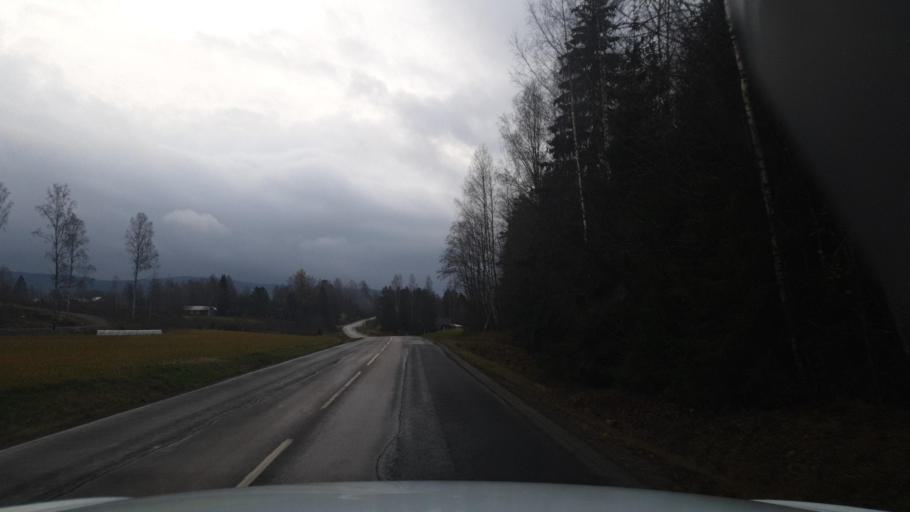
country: SE
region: Vaermland
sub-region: Arvika Kommun
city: Arvika
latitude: 59.8031
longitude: 12.6032
